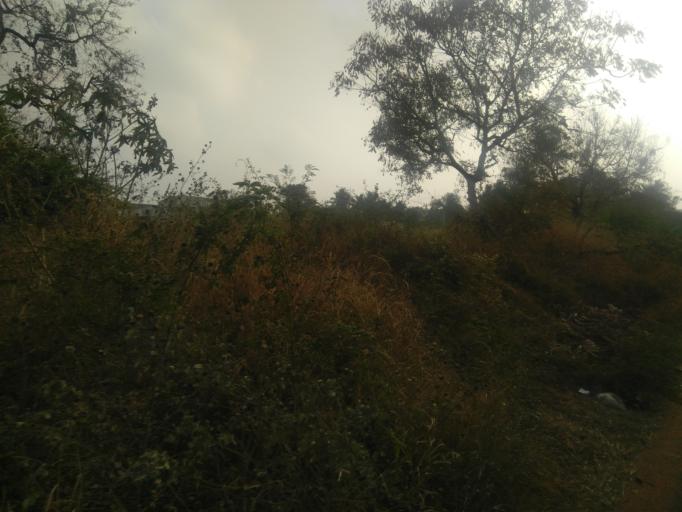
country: IN
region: Tamil Nadu
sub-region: Coimbatore
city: Perur
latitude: 11.0535
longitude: 76.8985
